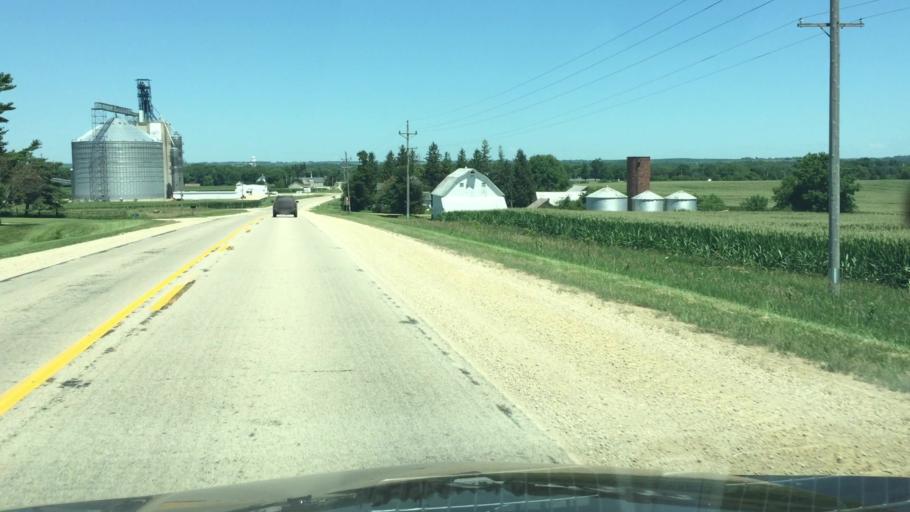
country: US
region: Iowa
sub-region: Cedar County
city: Mechanicsville
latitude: 41.9844
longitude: -91.1417
